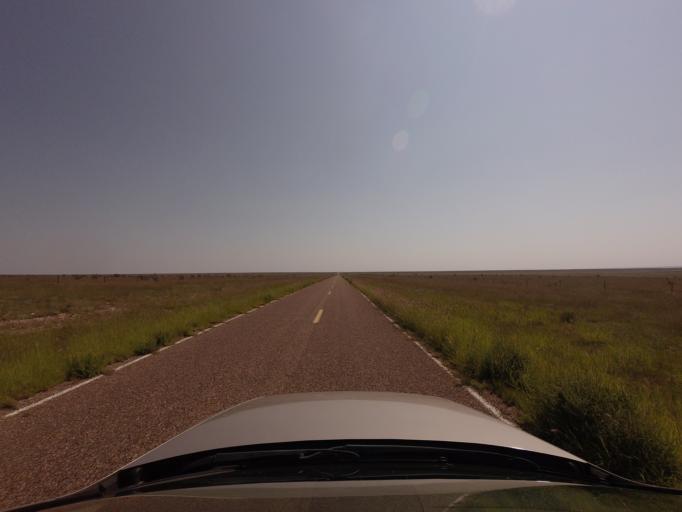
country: US
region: New Mexico
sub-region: Curry County
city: Cannon Air Force Base
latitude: 34.6331
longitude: -103.4108
